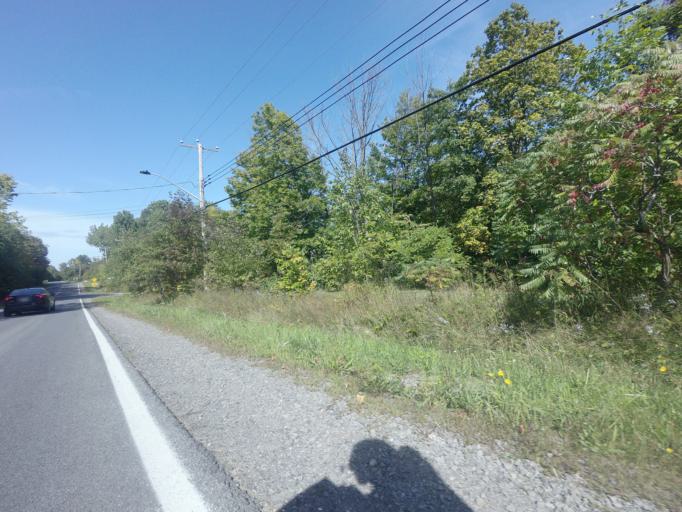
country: CA
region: Quebec
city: Dollard-Des Ormeaux
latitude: 45.5139
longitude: -73.8624
